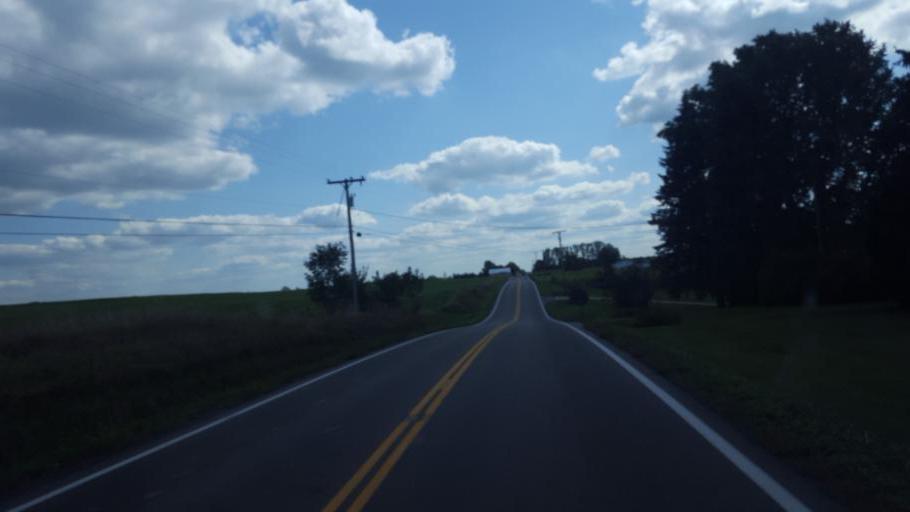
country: US
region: Ohio
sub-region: Ashland County
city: Ashland
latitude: 40.8970
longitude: -82.2119
